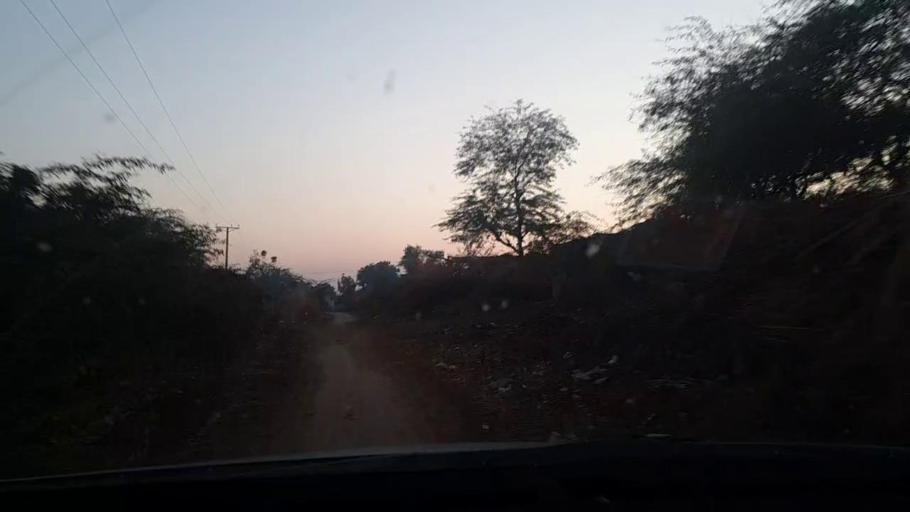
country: PK
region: Sindh
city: Tando Mittha Khan
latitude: 25.9284
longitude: 69.3316
